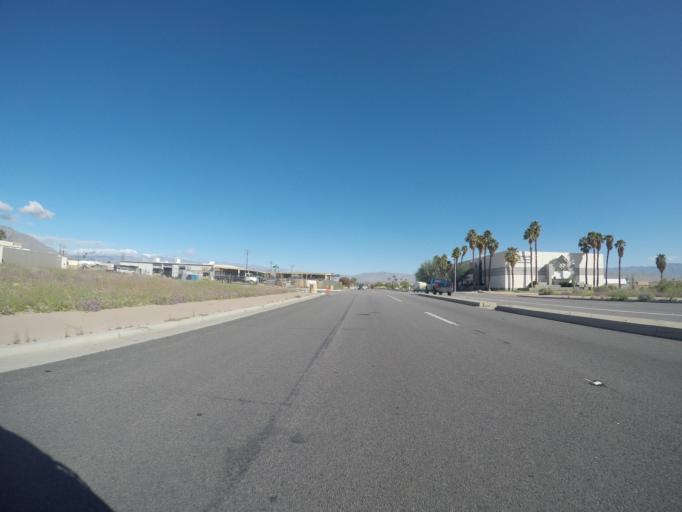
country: US
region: California
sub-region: Riverside County
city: Cathedral City
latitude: 33.8118
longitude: -116.4930
